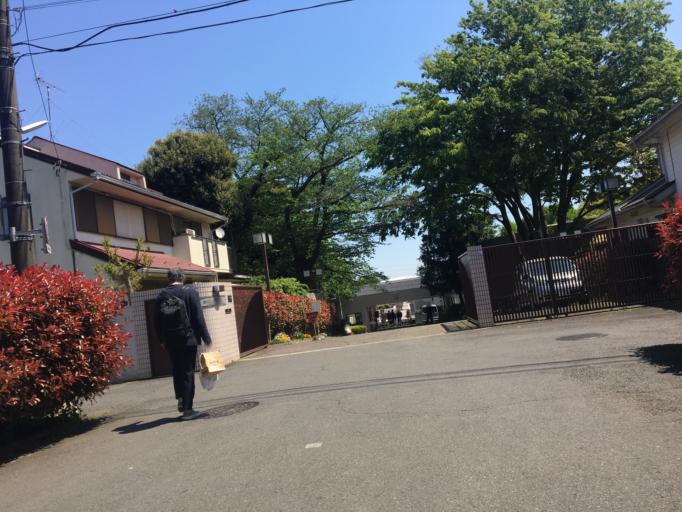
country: JP
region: Tokyo
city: Tanashicho
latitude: 35.7206
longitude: 139.5142
